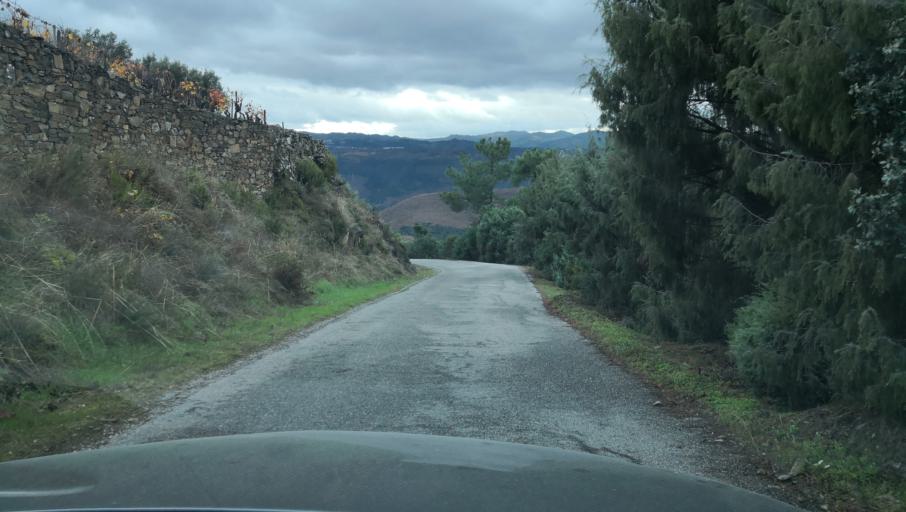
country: PT
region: Vila Real
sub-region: Sabrosa
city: Vilela
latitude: 41.1823
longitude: -7.5721
